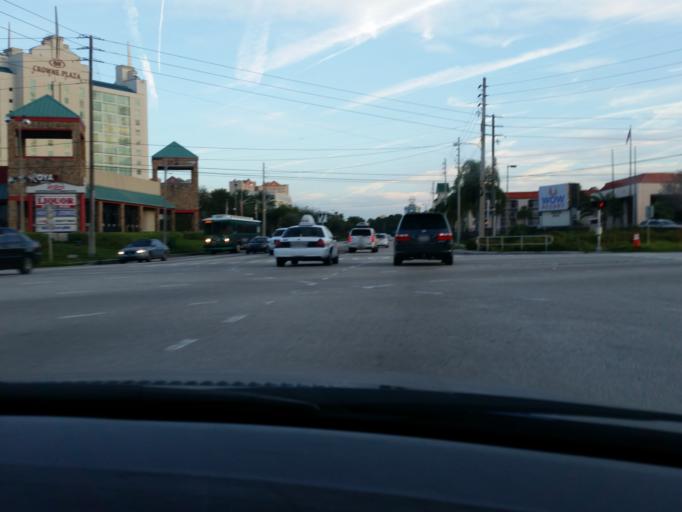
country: US
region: Florida
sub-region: Orange County
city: Tangelo Park
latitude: 28.4501
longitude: -81.4656
